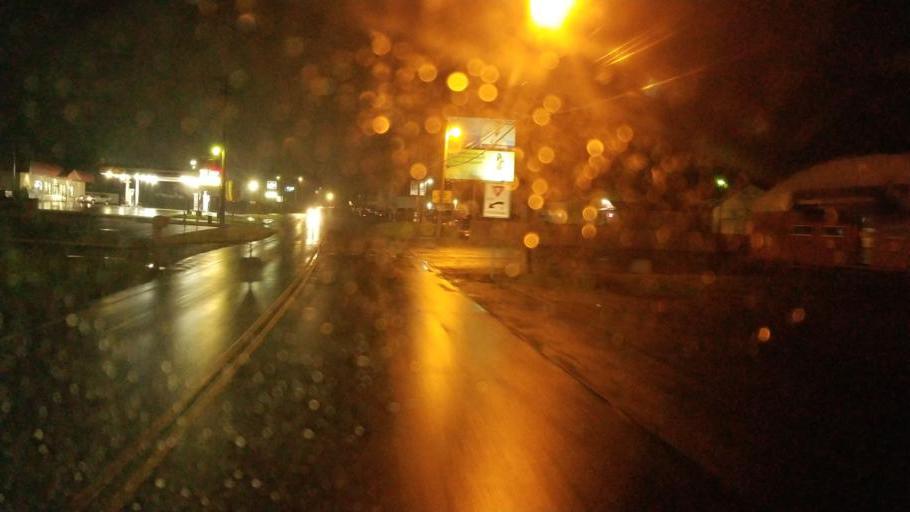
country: US
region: Ohio
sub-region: Highland County
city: Greenfield
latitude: 39.3478
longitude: -83.3999
